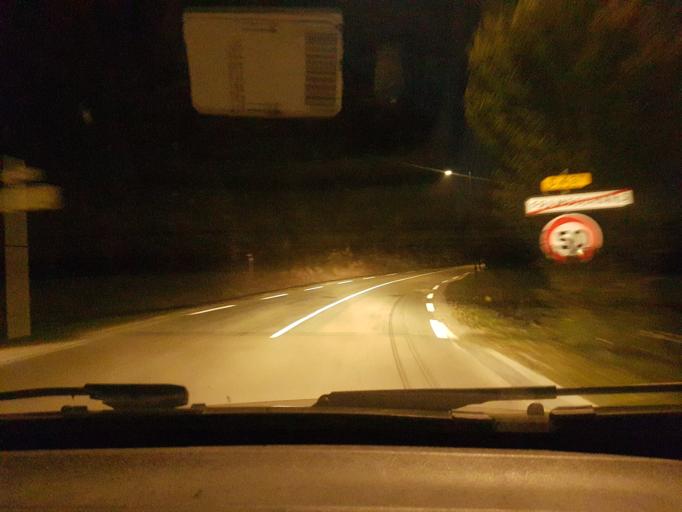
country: FR
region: Franche-Comte
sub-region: Departement du Doubs
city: Maiche
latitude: 47.2230
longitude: 6.7692
